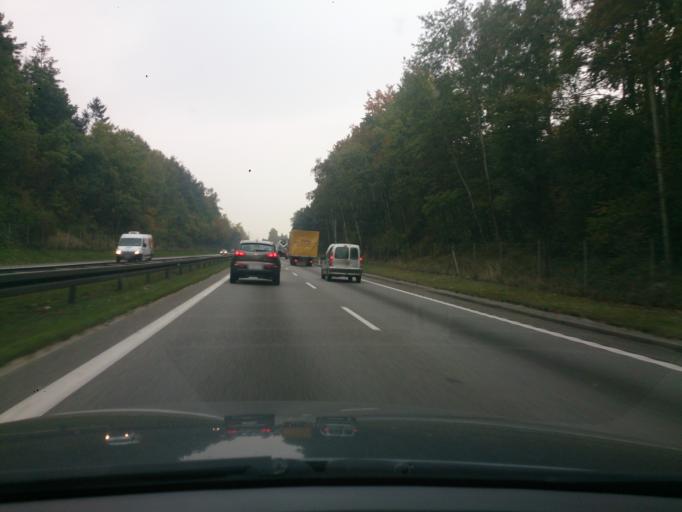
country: PL
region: Pomeranian Voivodeship
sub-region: Gdynia
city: Wielki Kack
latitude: 54.3897
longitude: 18.4948
